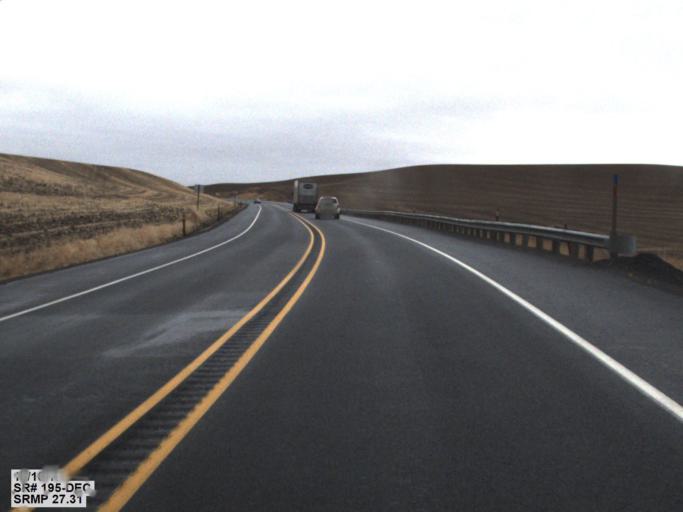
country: US
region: Washington
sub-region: Whitman County
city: Pullman
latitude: 46.7597
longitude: -117.2615
